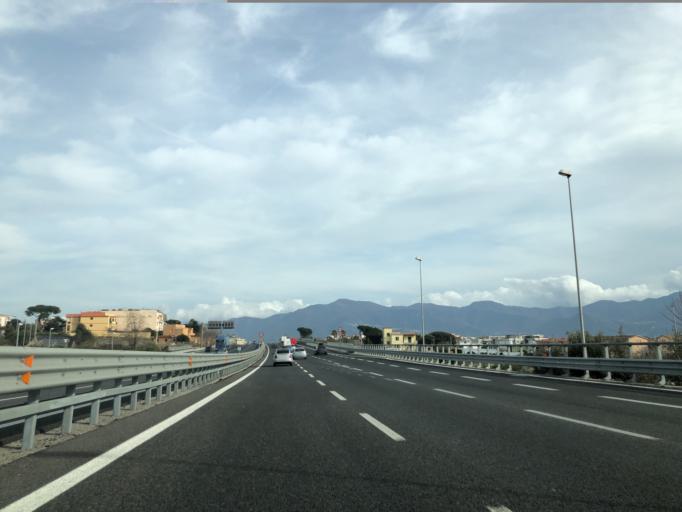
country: IT
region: Campania
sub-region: Provincia di Napoli
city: Trecase
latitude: 40.7662
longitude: 14.4318
